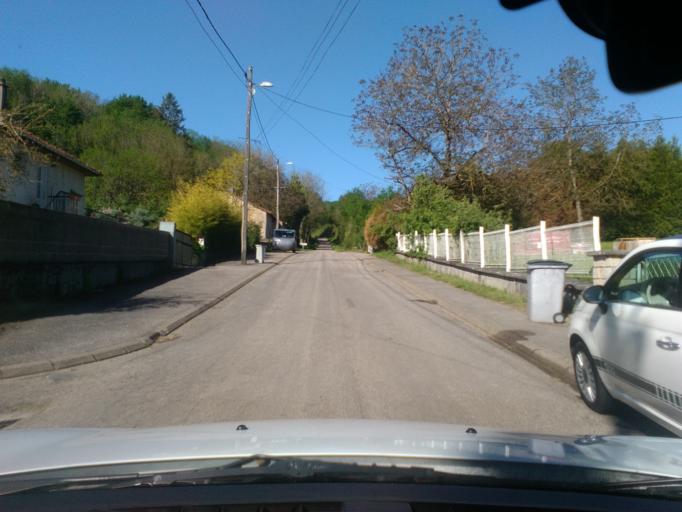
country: FR
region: Lorraine
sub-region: Departement des Vosges
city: Charmes
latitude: 48.3336
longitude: 6.2268
